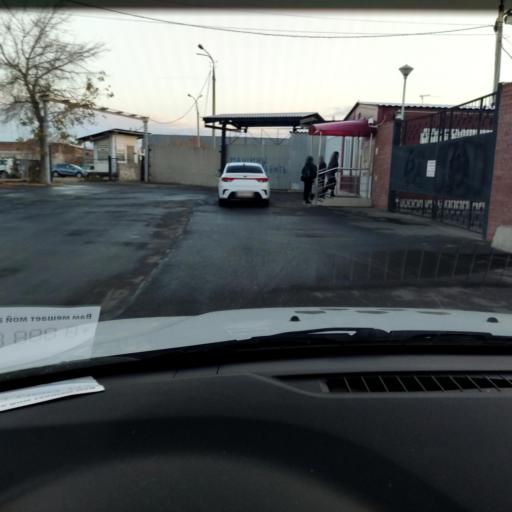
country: RU
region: Samara
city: Tol'yatti
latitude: 53.5479
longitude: 49.4371
